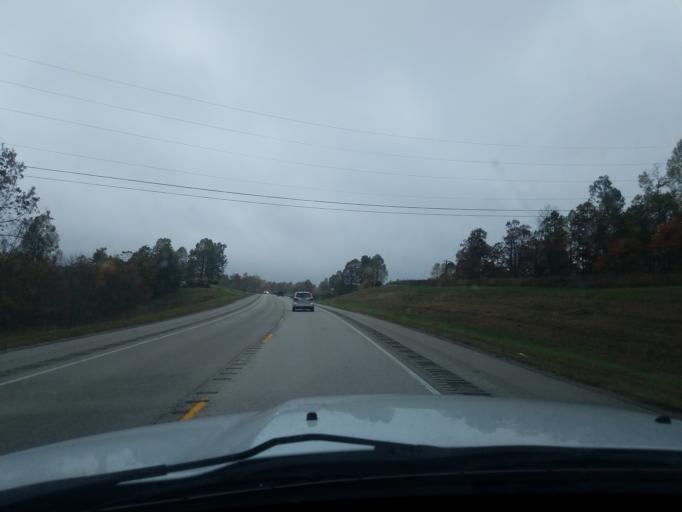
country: US
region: Kentucky
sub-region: Larue County
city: Hodgenville
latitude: 37.4646
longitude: -85.5713
